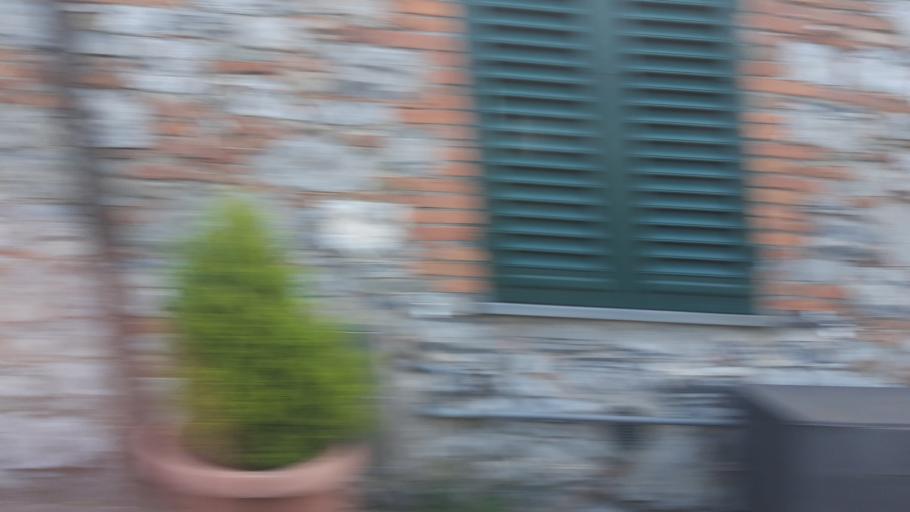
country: IT
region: Tuscany
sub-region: Provincia di Lucca
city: Capannori
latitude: 43.8641
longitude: 10.5585
